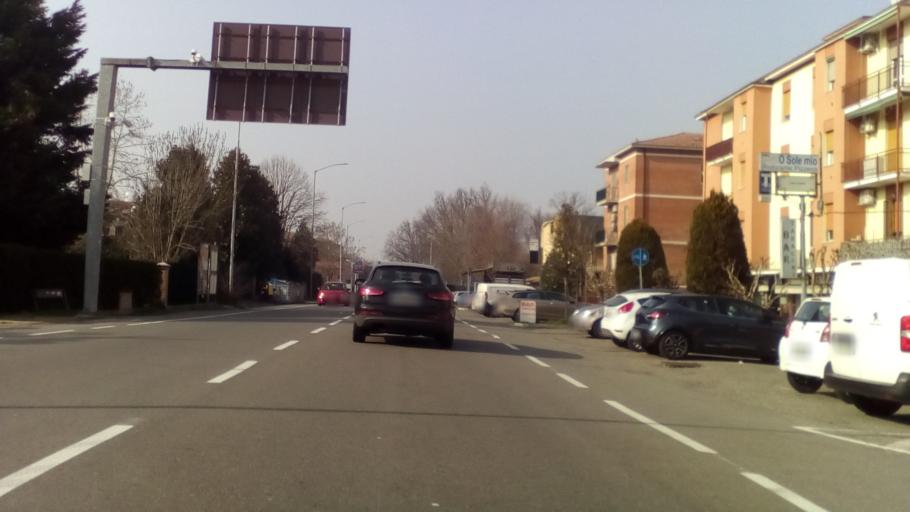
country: IT
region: Emilia-Romagna
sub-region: Provincia di Modena
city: Modena
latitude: 44.6261
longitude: 10.9491
